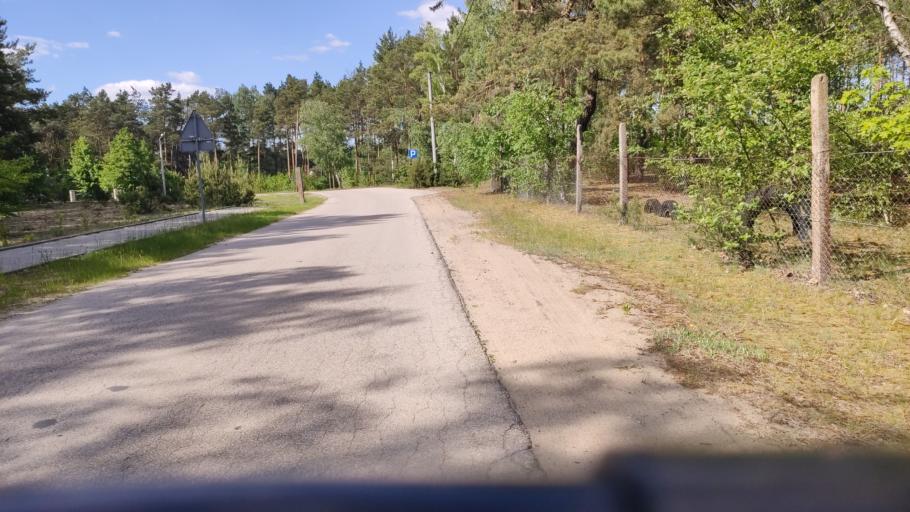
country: PL
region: Kujawsko-Pomorskie
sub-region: Wloclawek
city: Wloclawek
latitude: 52.5950
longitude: 19.0872
